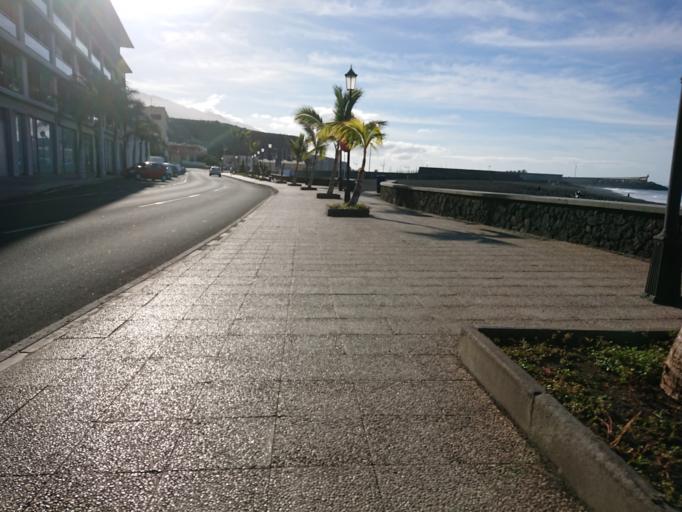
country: ES
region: Canary Islands
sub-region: Provincia de Santa Cruz de Tenerife
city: Tazacorte
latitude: 28.6491
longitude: -17.9451
